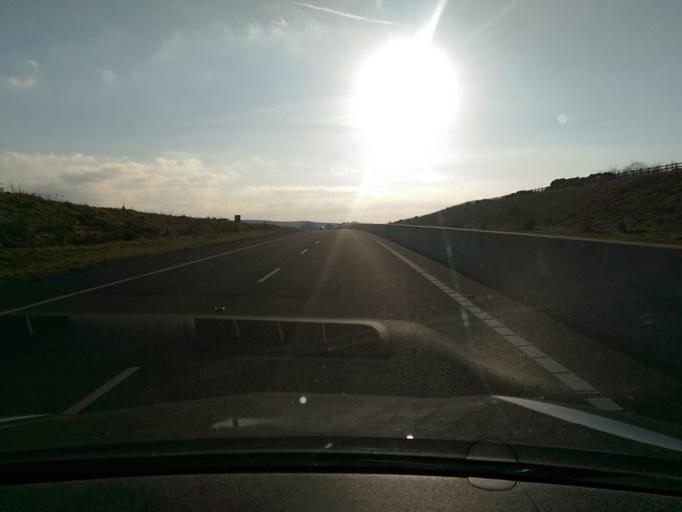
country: IE
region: Munster
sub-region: North Tipperary
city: Roscrea
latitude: 52.9139
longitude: -7.8289
